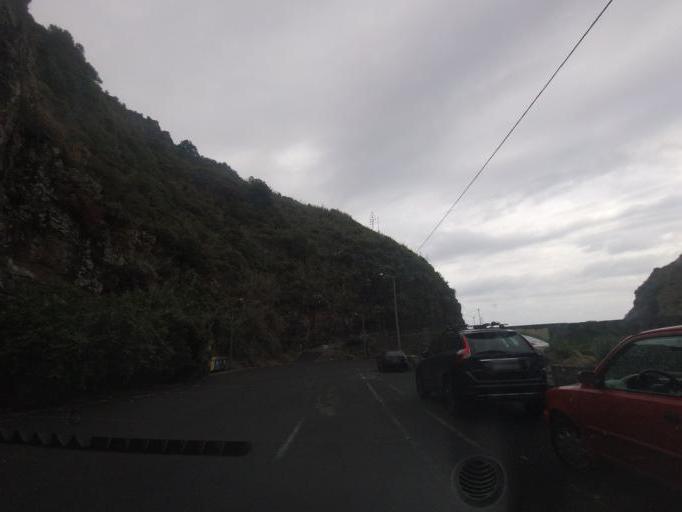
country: PT
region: Madeira
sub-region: Santana
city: Santana
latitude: 32.8280
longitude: -16.8978
